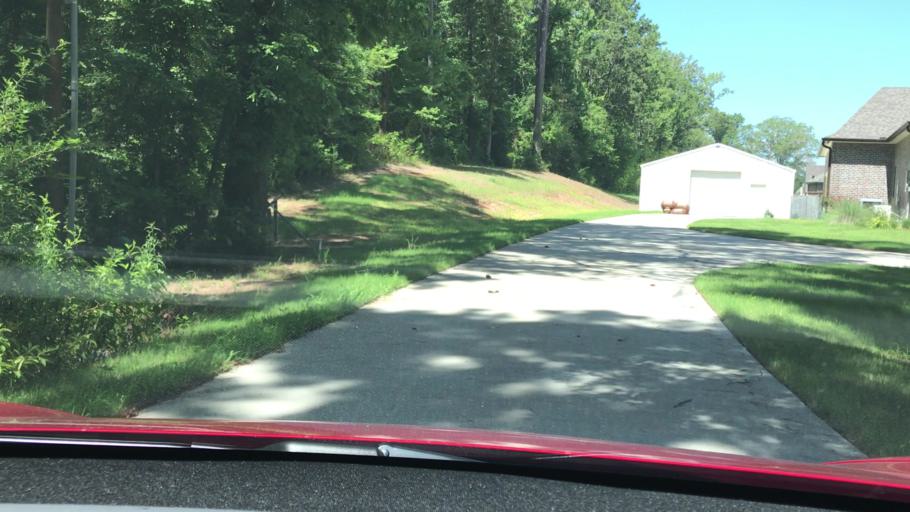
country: US
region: Louisiana
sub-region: De Soto Parish
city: Stonewall
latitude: 32.3404
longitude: -93.7088
